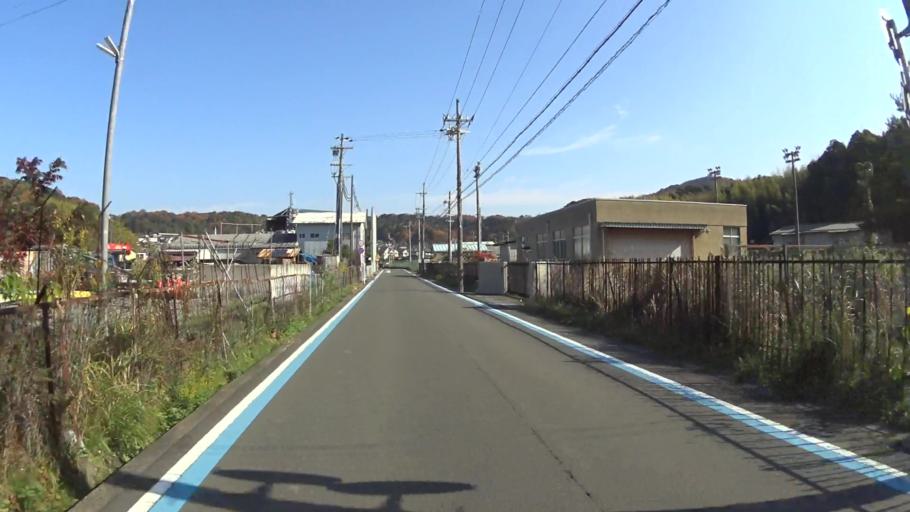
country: JP
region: Kyoto
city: Maizuru
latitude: 35.4749
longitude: 135.3458
